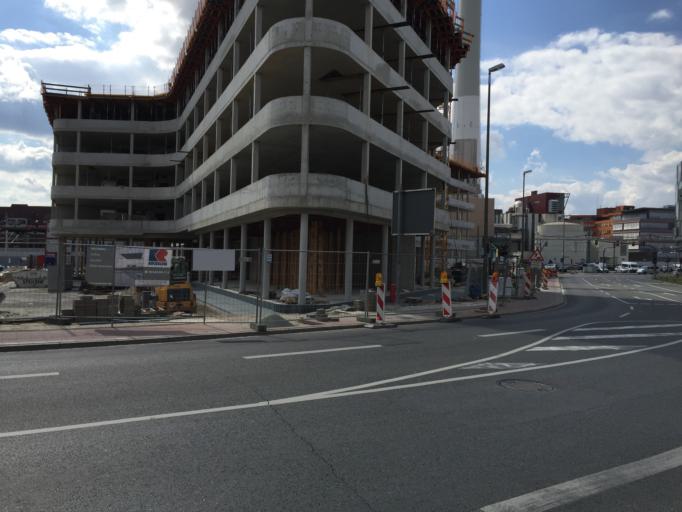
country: DE
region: Bavaria
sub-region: Regierungsbezirk Mittelfranken
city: Erlangen
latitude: 49.5917
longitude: 11.0045
